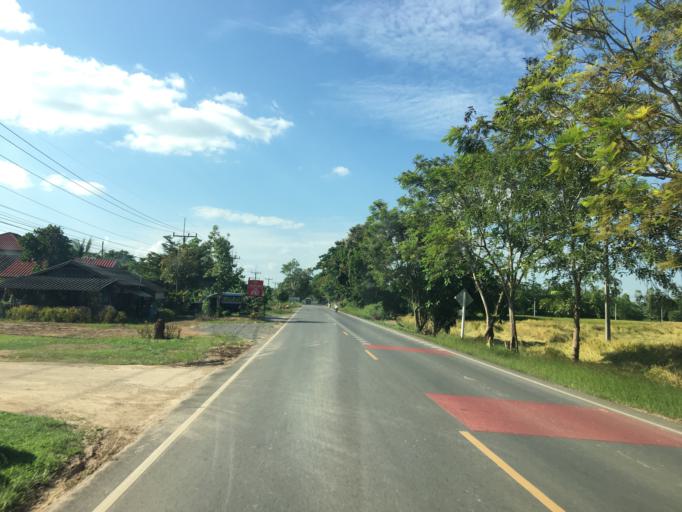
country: TH
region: Phayao
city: Chun
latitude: 19.3273
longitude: 100.1440
